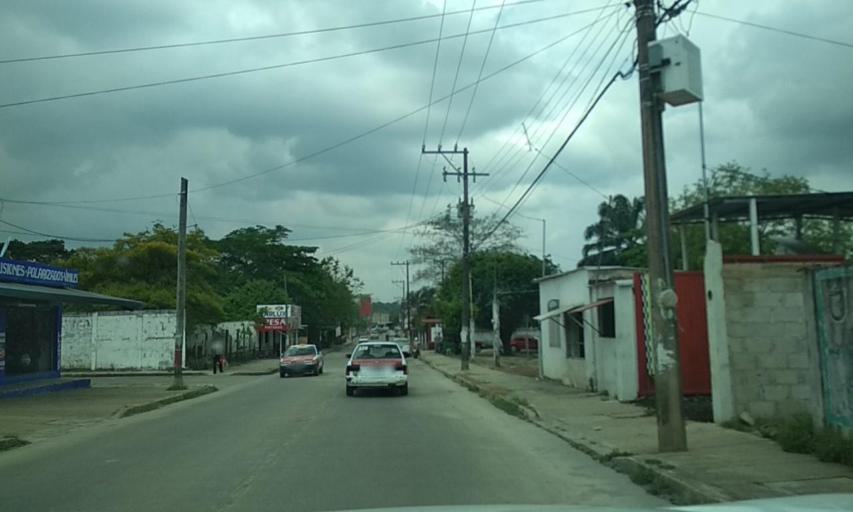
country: MX
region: Veracruz
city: Las Choapas
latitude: 17.9008
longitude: -94.0969
